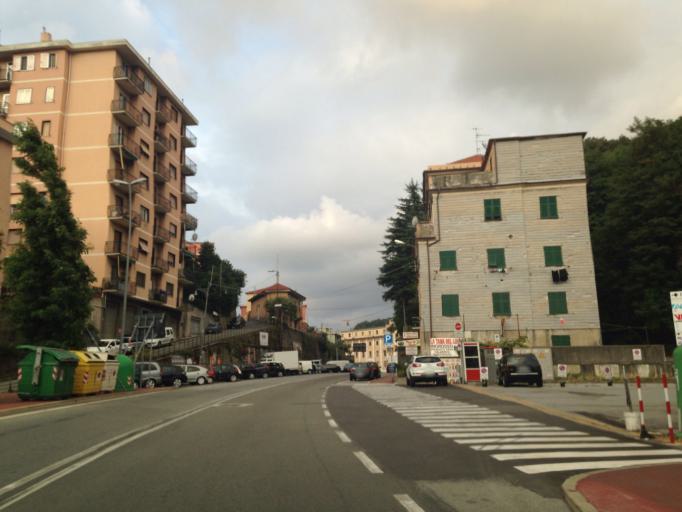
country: IT
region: Liguria
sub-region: Provincia di Genova
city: Manesseno
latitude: 44.4643
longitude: 8.9039
